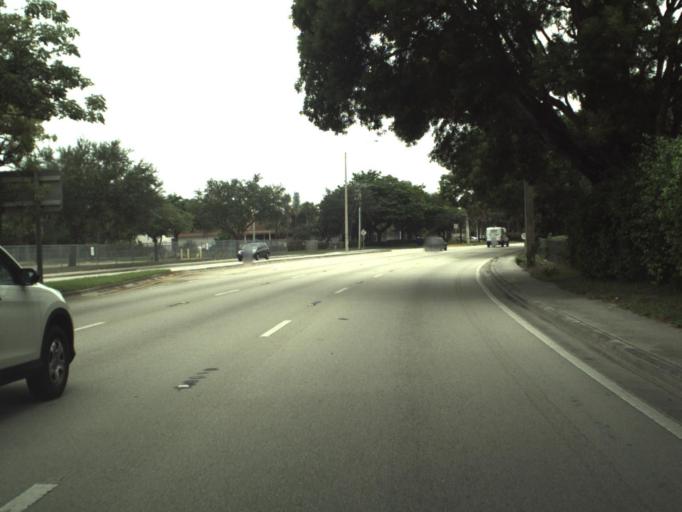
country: US
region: Florida
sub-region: Broward County
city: Plantation
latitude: 26.1370
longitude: -80.2377
